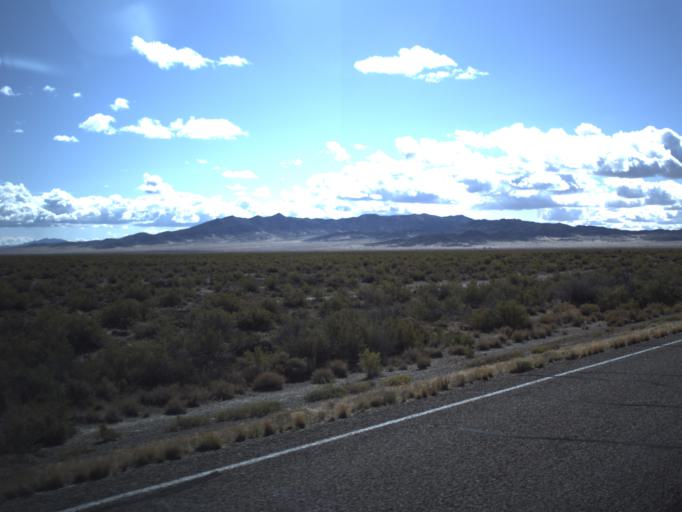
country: US
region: Nevada
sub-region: White Pine County
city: McGill
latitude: 39.0445
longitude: -114.0362
